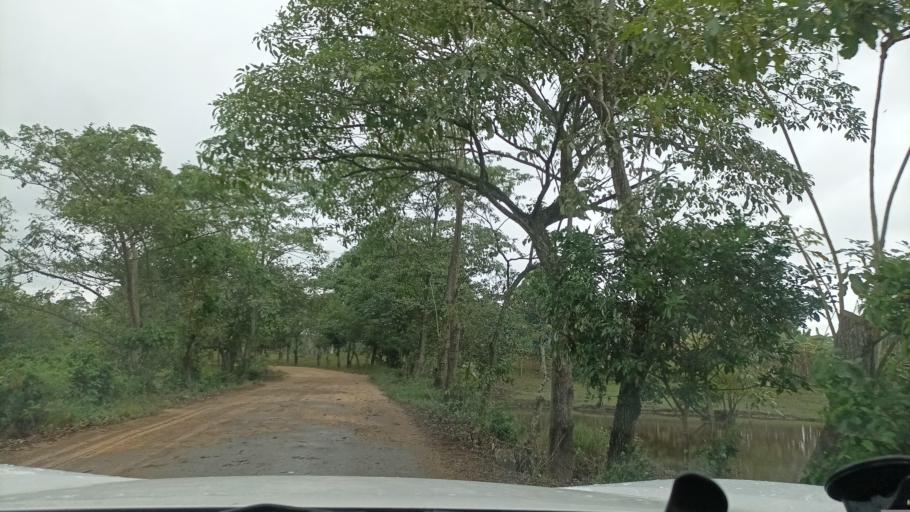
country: MX
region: Veracruz
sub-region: Moloacan
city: Cuichapa
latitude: 17.7799
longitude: -94.3884
